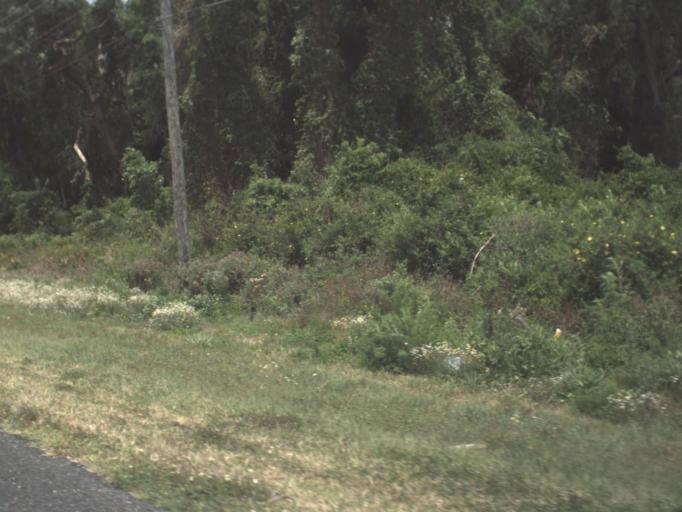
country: US
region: Florida
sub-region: Sumter County
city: Wildwood
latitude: 28.8327
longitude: -82.0003
